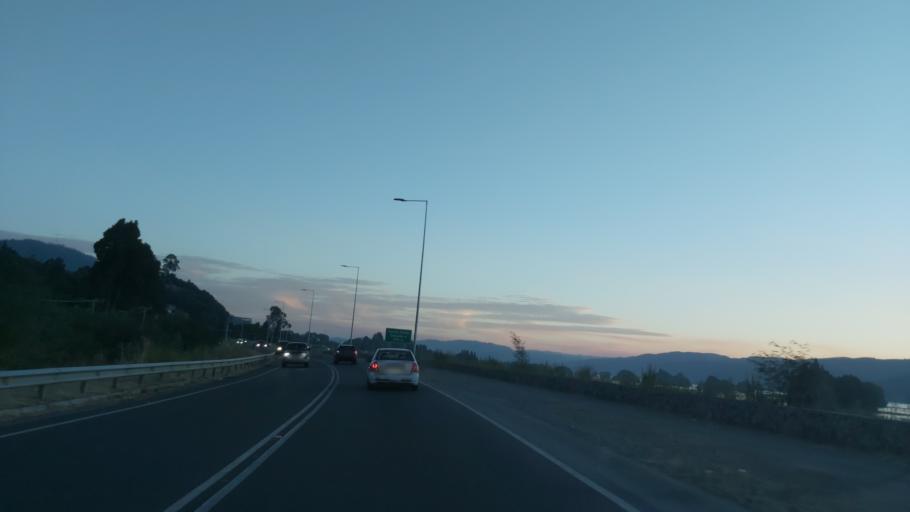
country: CL
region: Biobio
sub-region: Provincia de Concepcion
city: Chiguayante
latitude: -36.8876
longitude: -73.0381
